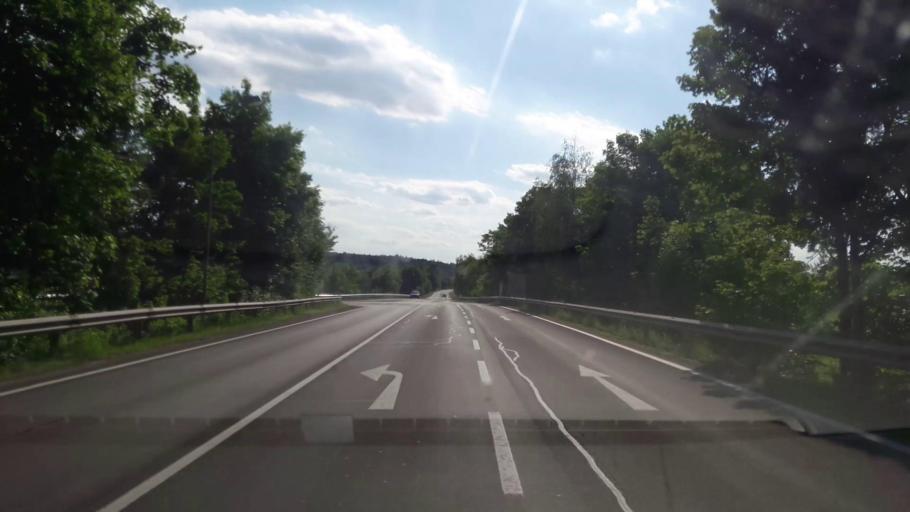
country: AT
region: Styria
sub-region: Politischer Bezirk Suedoststeiermark
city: Fehring
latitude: 46.9422
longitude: 16.0105
